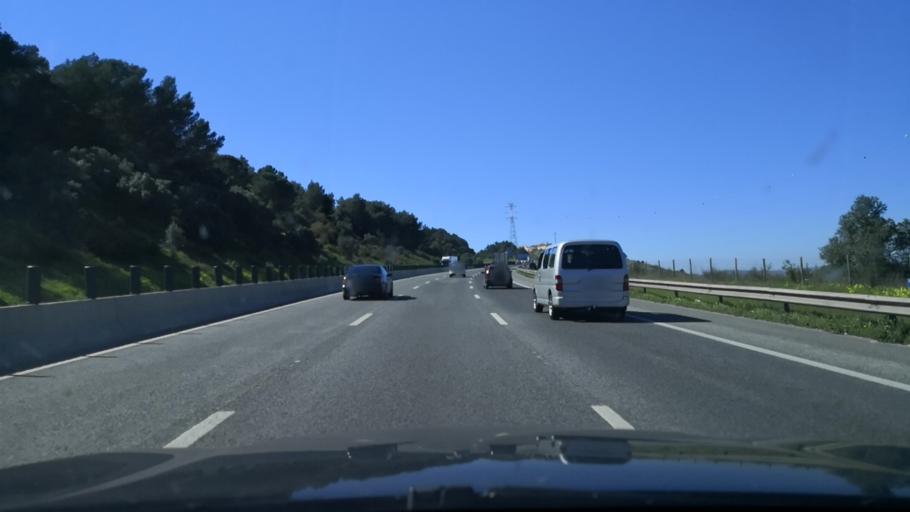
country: PT
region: Lisbon
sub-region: Vila Franca de Xira
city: Vialonga
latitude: 38.8692
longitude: -9.0721
